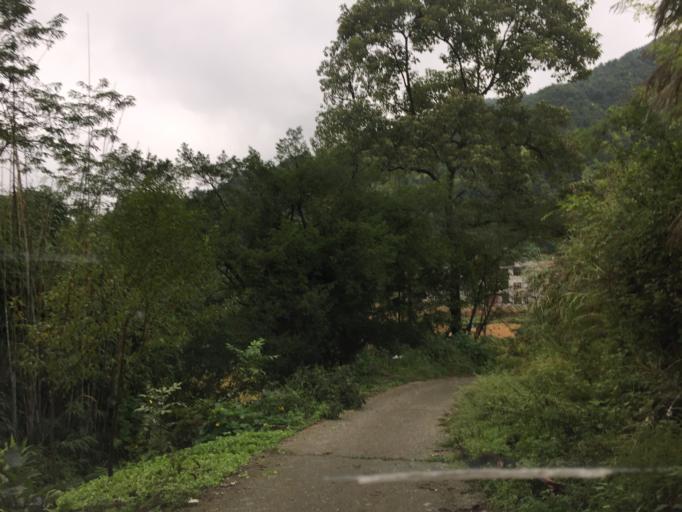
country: CN
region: Guizhou Sheng
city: Longquan
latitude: 28.2119
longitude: 108.0551
